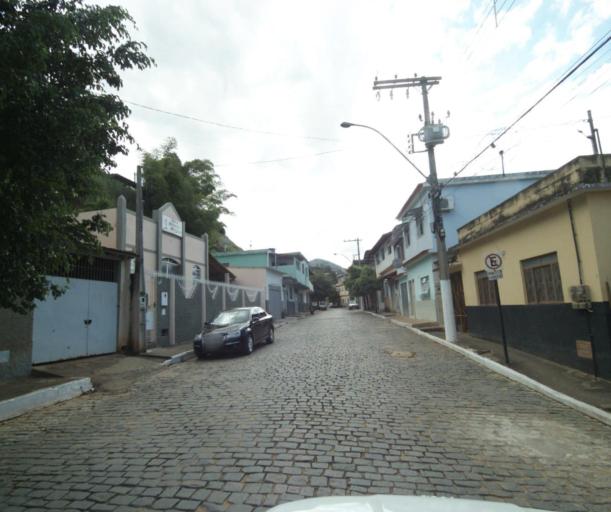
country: BR
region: Espirito Santo
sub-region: Sao Jose Do Calcado
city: Sao Jose do Calcado
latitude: -21.0267
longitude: -41.6572
